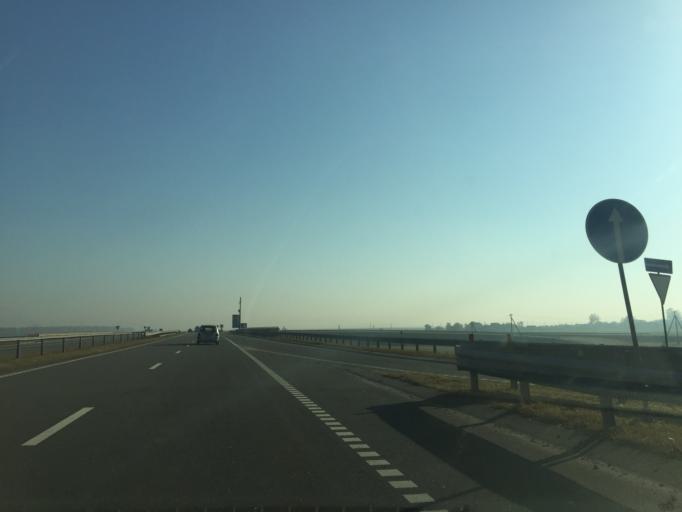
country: BY
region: Gomel
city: Kastsyukowka
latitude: 52.4892
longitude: 30.8162
